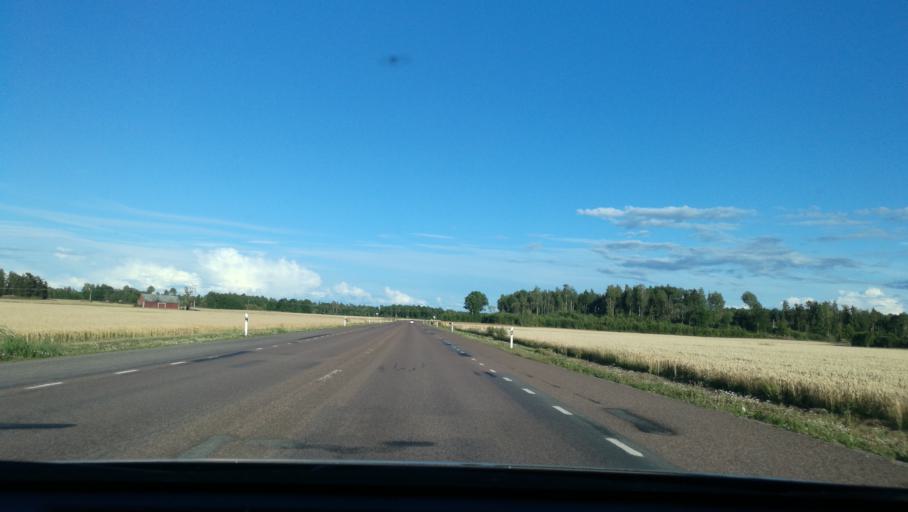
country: SE
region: Vaestmanland
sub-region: Kopings Kommun
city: Koping
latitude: 59.4586
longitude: 16.0099
